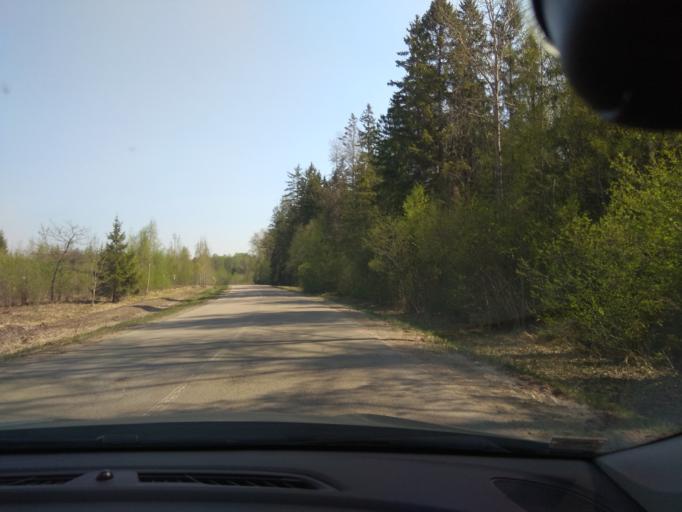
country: LT
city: Linkuva
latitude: 55.9816
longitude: 24.1805
